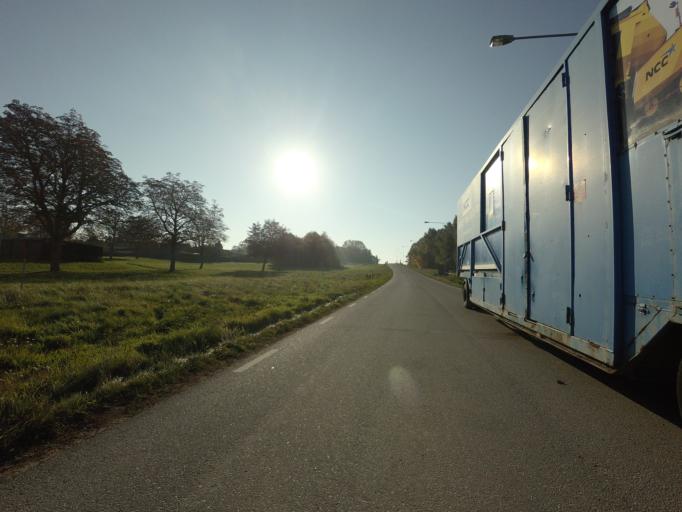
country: SE
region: Skane
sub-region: Burlovs Kommun
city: Arloev
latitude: 55.6489
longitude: 13.1007
